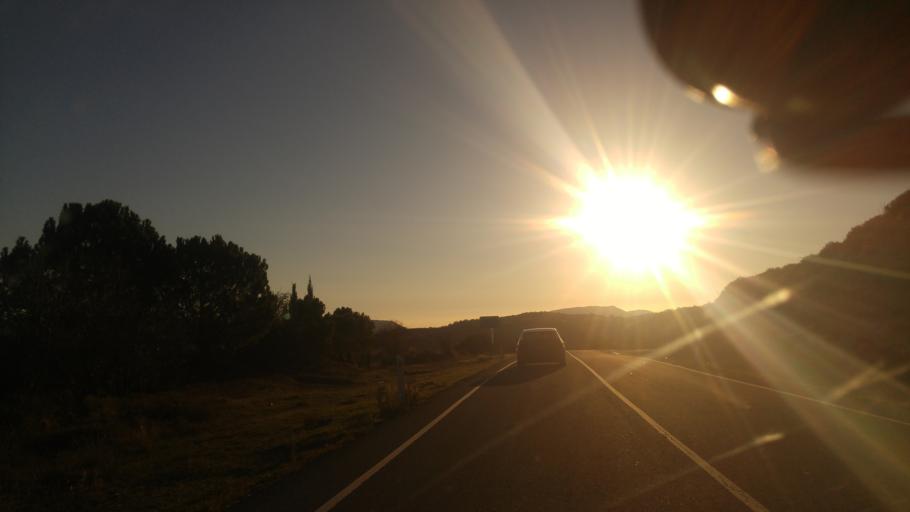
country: CY
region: Limassol
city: Pachna
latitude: 34.8179
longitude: 32.7968
